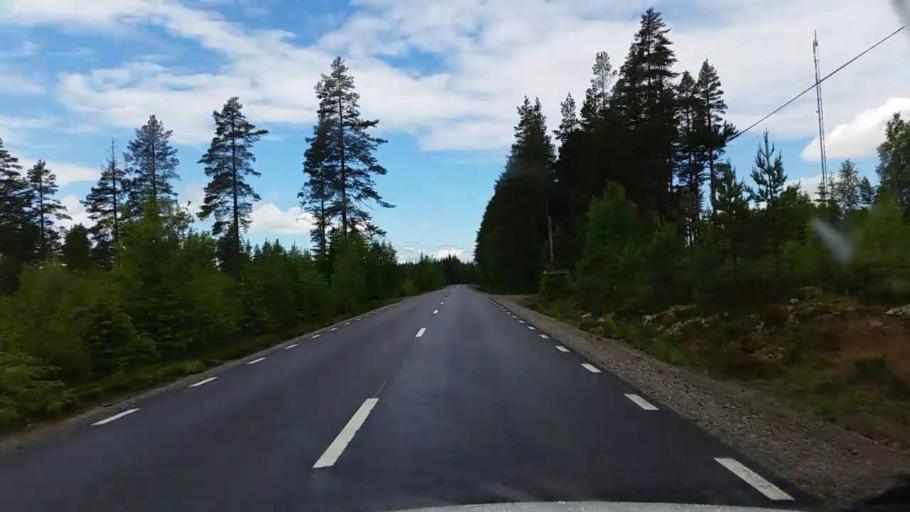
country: SE
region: Gaevleborg
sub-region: Sandvikens Kommun
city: Jarbo
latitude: 60.8487
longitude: 16.4558
